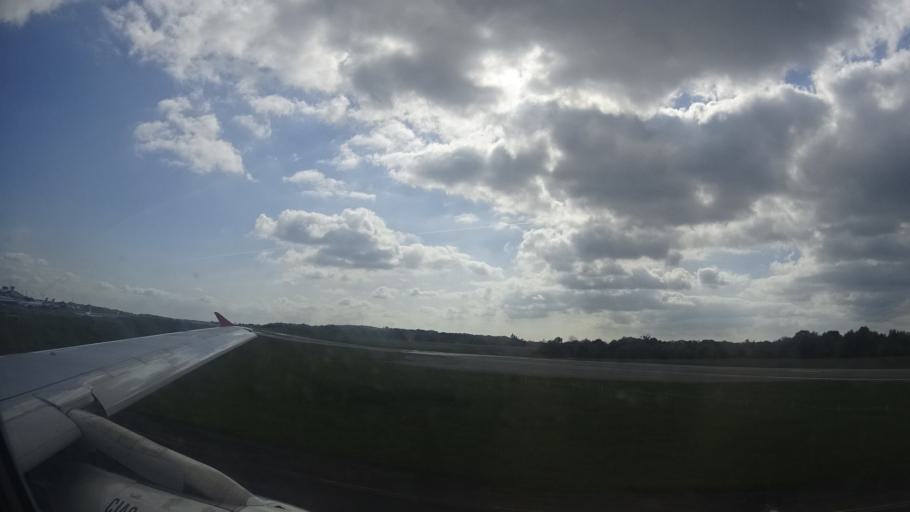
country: FR
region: Pays de la Loire
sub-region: Departement de la Loire-Atlantique
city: Bouguenais
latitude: 47.1638
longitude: -1.6006
